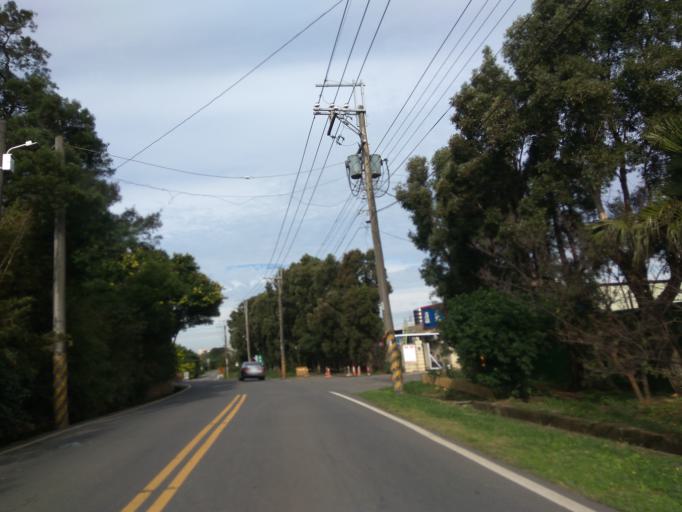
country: TW
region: Taiwan
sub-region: Hsinchu
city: Zhubei
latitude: 24.9565
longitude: 121.1214
